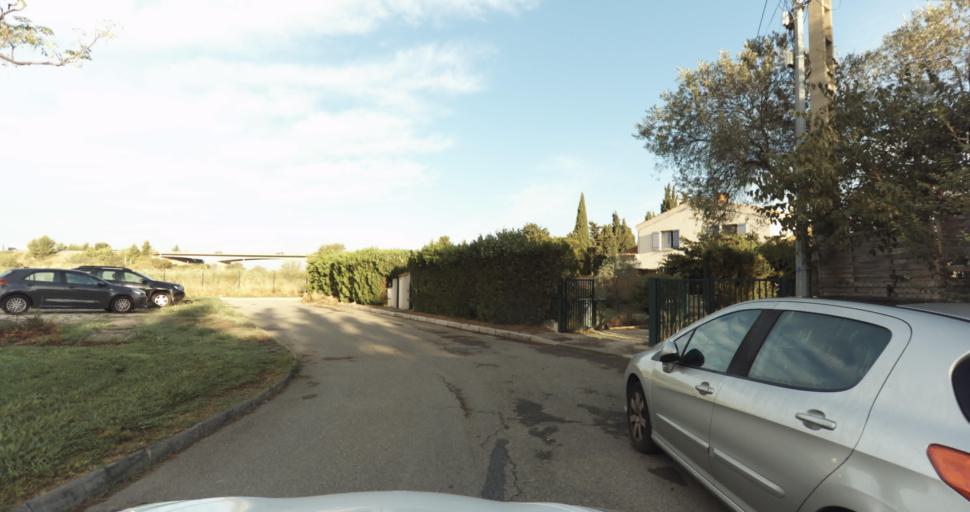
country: FR
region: Provence-Alpes-Cote d'Azur
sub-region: Departement des Bouches-du-Rhone
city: Miramas
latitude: 43.5843
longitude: 4.9902
